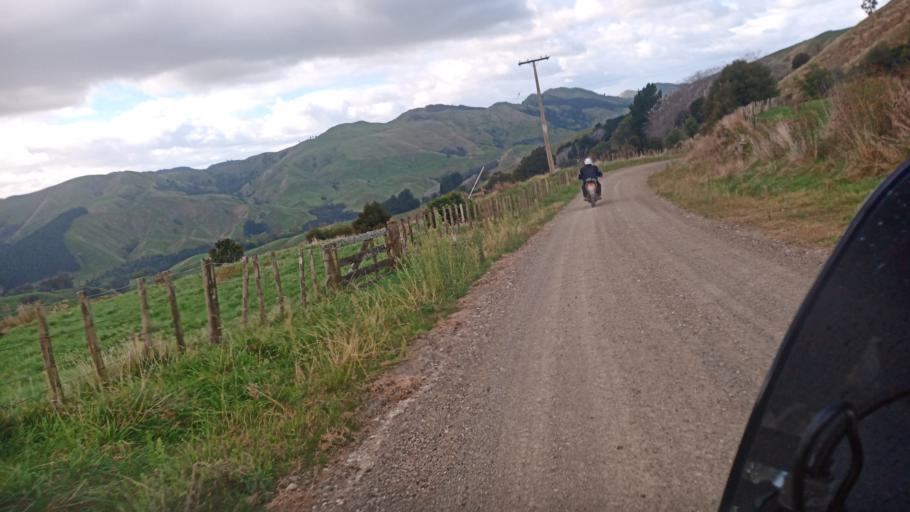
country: NZ
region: Gisborne
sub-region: Gisborne District
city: Gisborne
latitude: -38.4646
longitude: 177.6232
